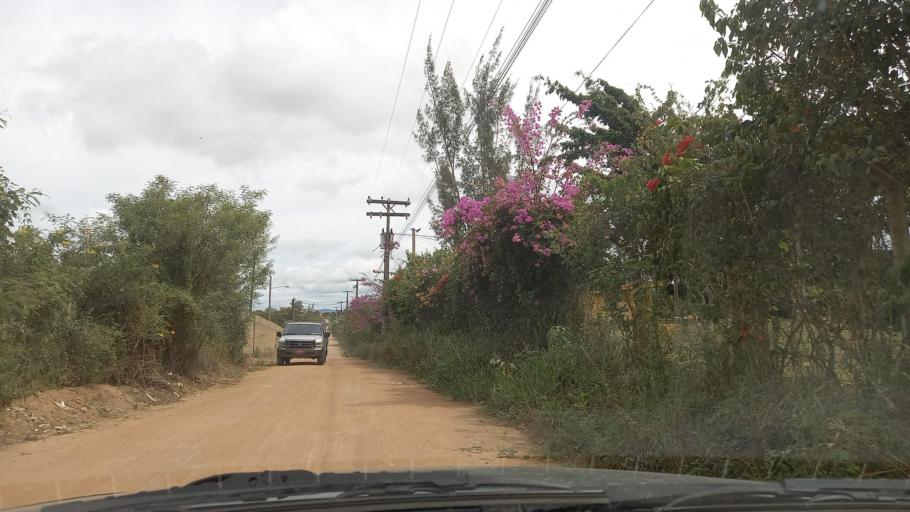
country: BR
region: Pernambuco
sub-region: Gravata
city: Gravata
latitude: -8.1916
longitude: -35.5916
